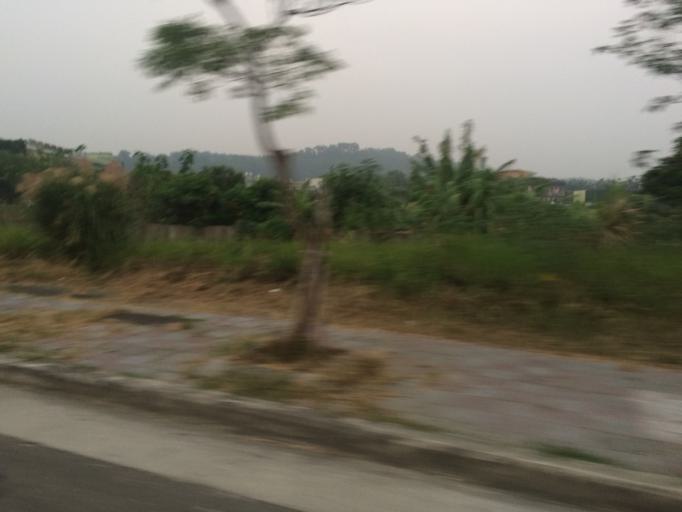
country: TW
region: Taiwan
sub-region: Hsinchu
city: Hsinchu
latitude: 24.7264
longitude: 120.9184
